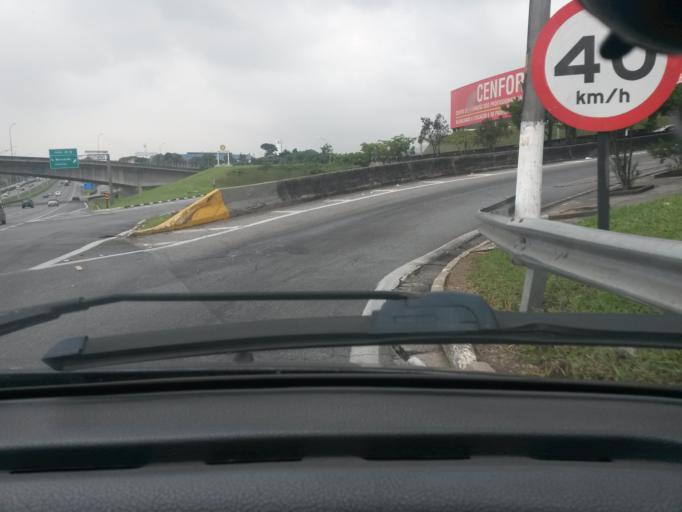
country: BR
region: Sao Paulo
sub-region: Sao Bernardo Do Campo
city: Sao Bernardo do Campo
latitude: -23.7070
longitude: -46.5618
